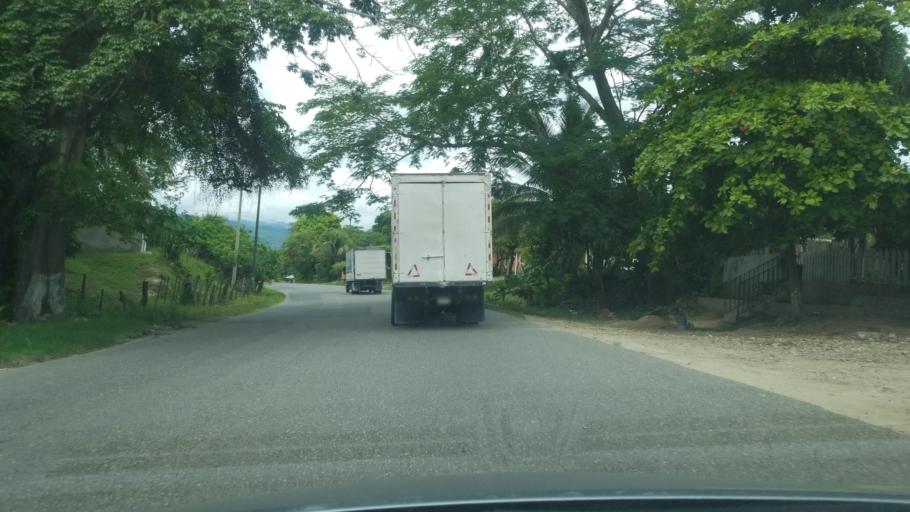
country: HN
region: Santa Barbara
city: San Marcos
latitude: 15.3120
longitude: -88.4392
